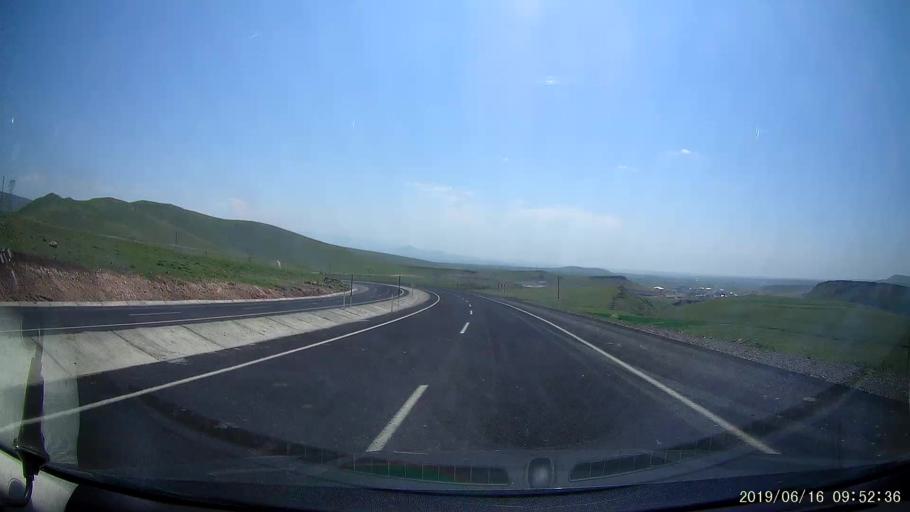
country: TR
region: Kars
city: Digor
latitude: 40.3937
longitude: 43.3905
